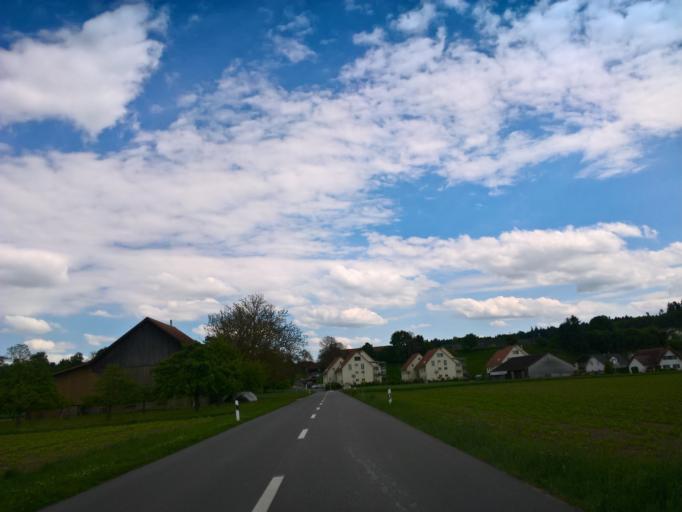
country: CH
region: Zurich
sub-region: Bezirk Buelach
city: Freienstein
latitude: 47.5796
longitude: 8.6106
